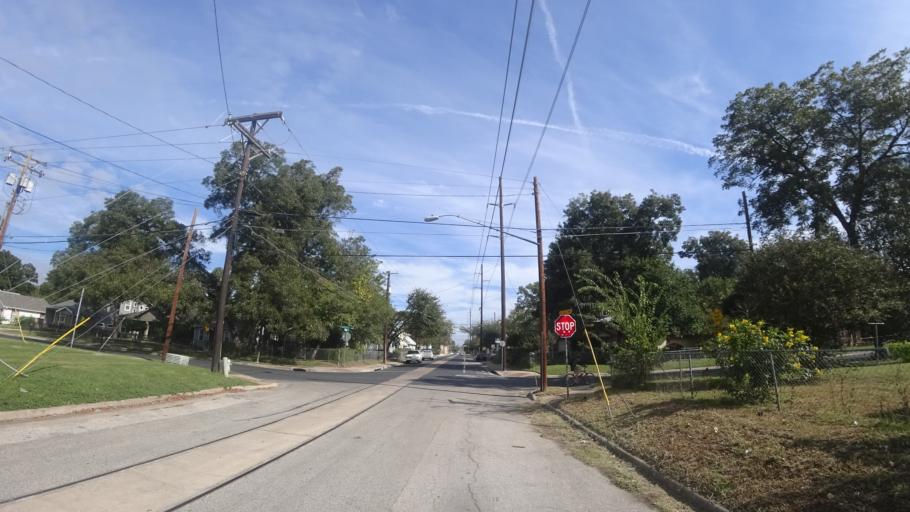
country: US
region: Texas
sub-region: Travis County
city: Austin
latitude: 30.2524
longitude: -97.7176
